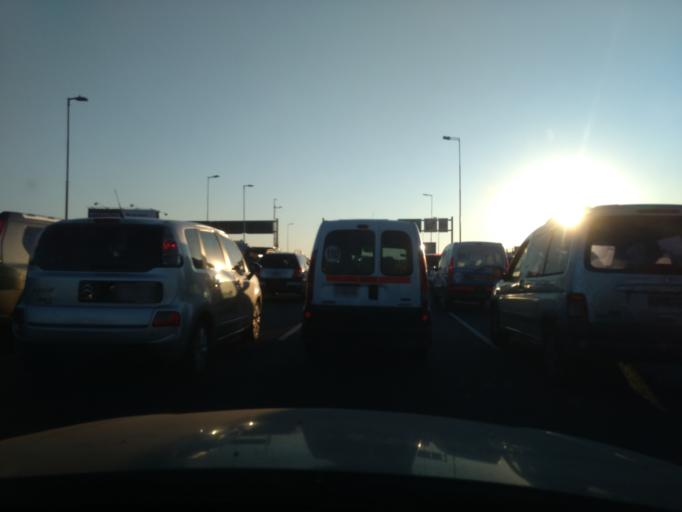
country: AR
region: Buenos Aires F.D.
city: Villa Santa Rita
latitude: -34.6418
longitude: -58.4604
